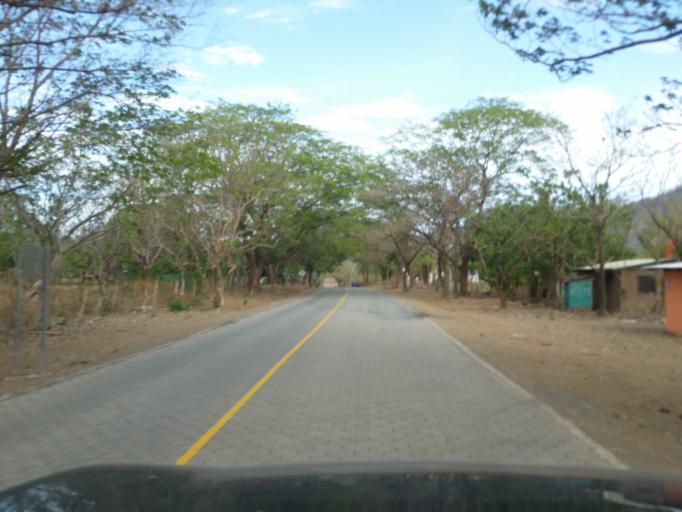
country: NI
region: Rivas
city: Tola
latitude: 11.4003
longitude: -85.9952
